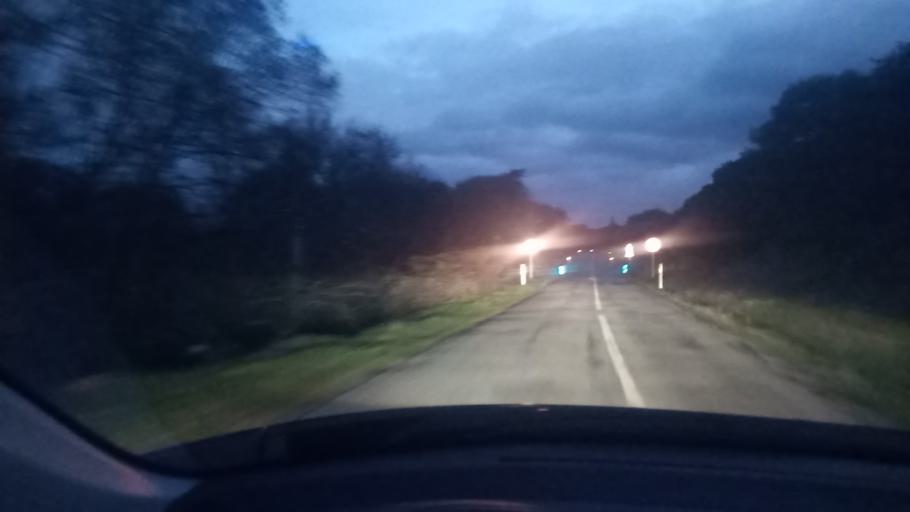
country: ES
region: Madrid
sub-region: Provincia de Madrid
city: Colmenar del Arroyo
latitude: 40.4368
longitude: -4.2237
